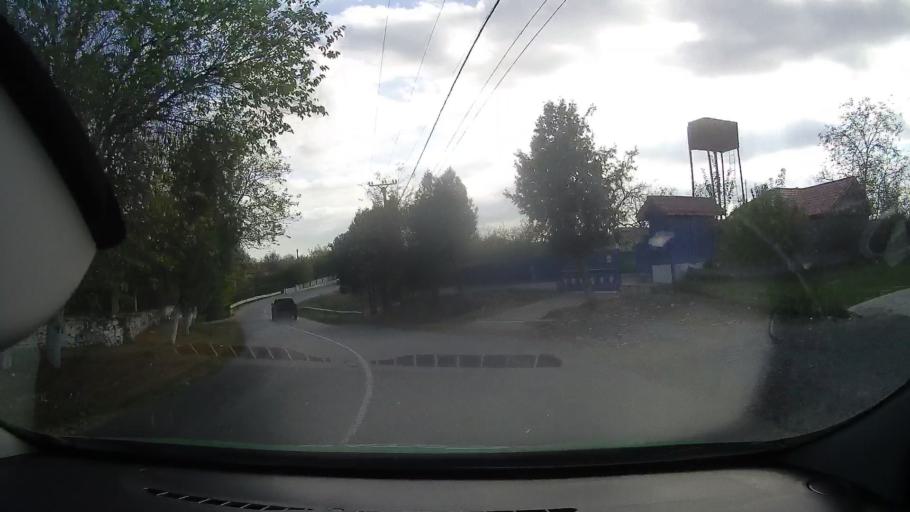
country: RO
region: Constanta
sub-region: Comuna Sacele
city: Sacele
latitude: 44.4862
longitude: 28.6448
